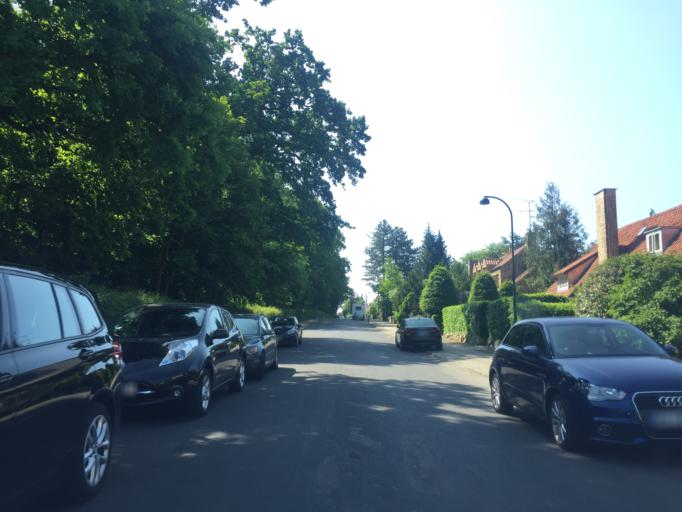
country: DK
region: Capital Region
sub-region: Lyngby-Tarbaek Kommune
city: Kongens Lyngby
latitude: 55.7590
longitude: 12.5445
